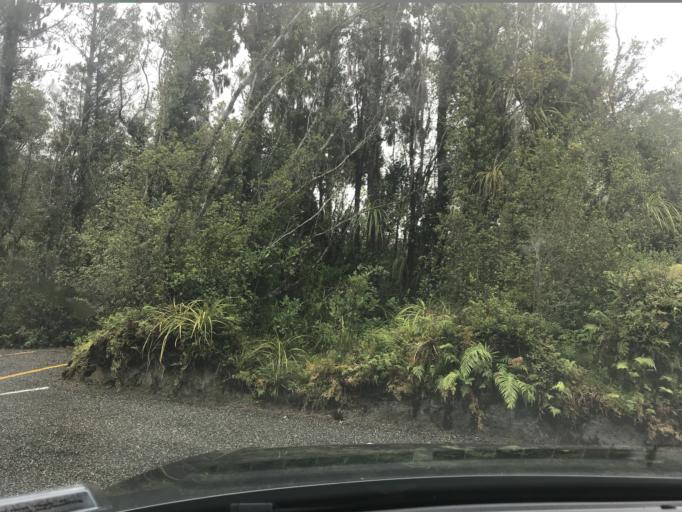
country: NZ
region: West Coast
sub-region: Westland District
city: Hokitika
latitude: -42.9565
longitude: 171.0199
